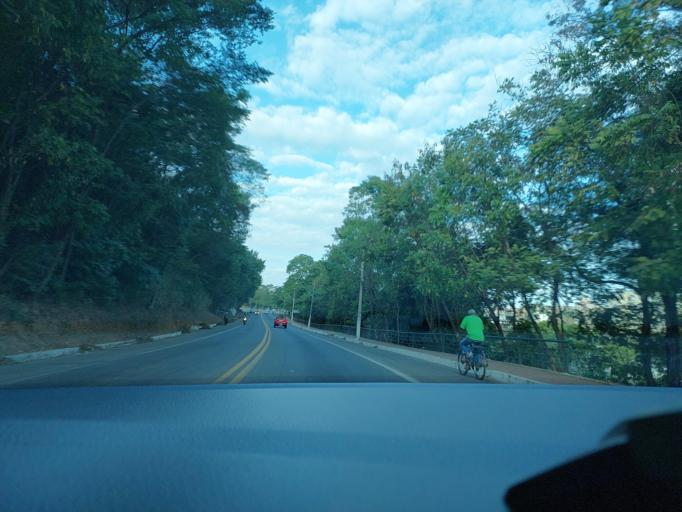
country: BR
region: Minas Gerais
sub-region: Muriae
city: Muriae
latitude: -21.1284
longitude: -42.3667
